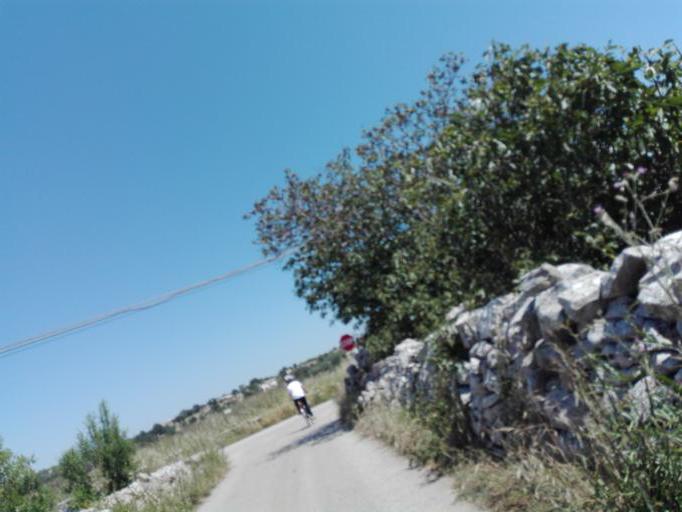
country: IT
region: Apulia
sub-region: Provincia di Bari
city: Putignano
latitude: 40.8434
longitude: 17.0968
